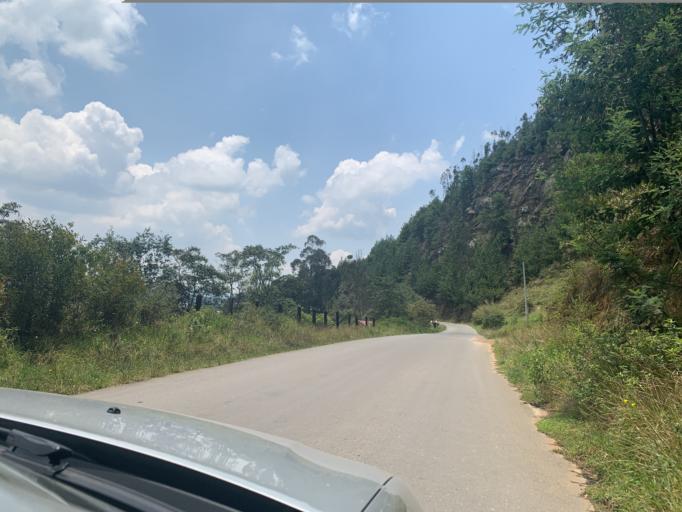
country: CO
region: Boyaca
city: Chiquinquira
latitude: 5.5442
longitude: -73.7509
